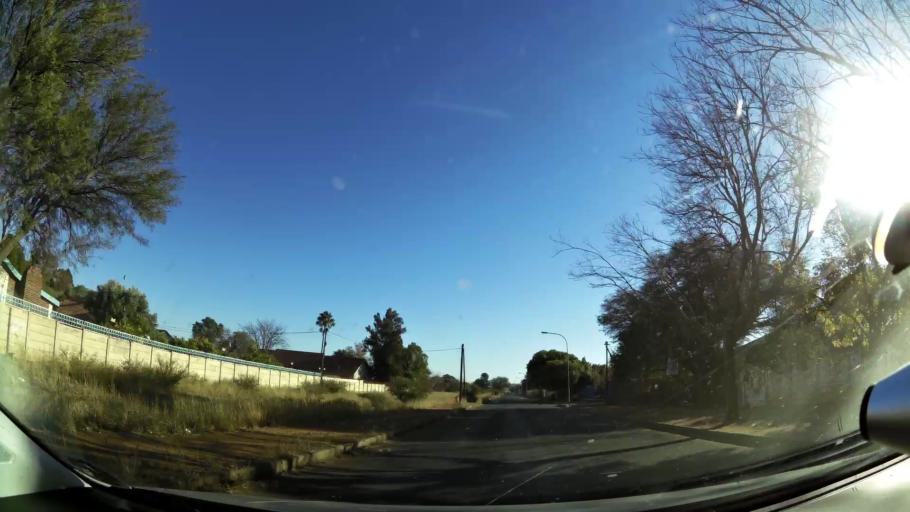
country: ZA
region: Northern Cape
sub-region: Frances Baard District Municipality
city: Kimberley
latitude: -28.7396
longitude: 24.7308
